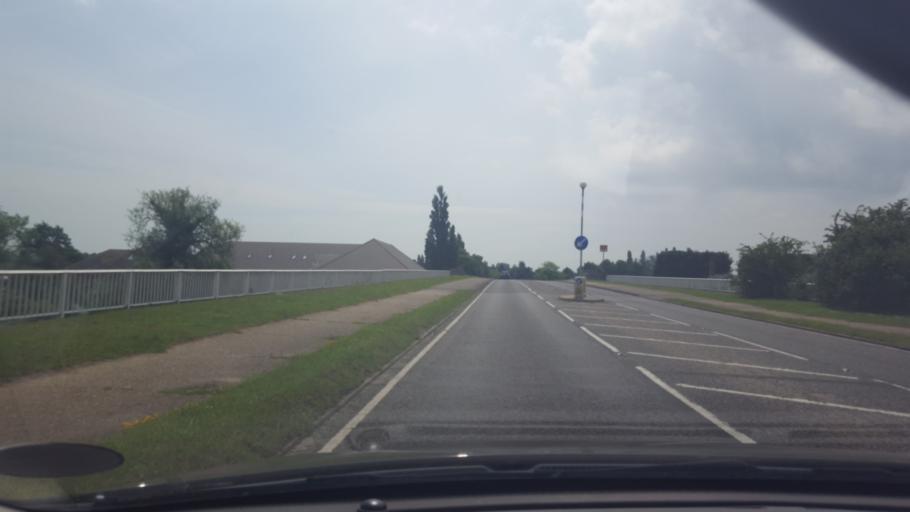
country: GB
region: England
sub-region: Essex
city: Little Clacton
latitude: 51.8542
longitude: 1.1158
